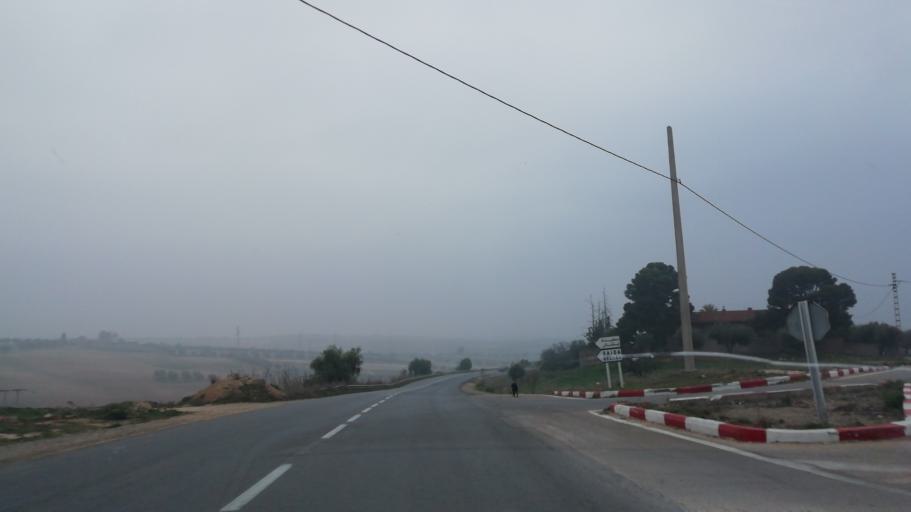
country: DZ
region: Mascara
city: Mascara
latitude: 35.4115
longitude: 0.1586
